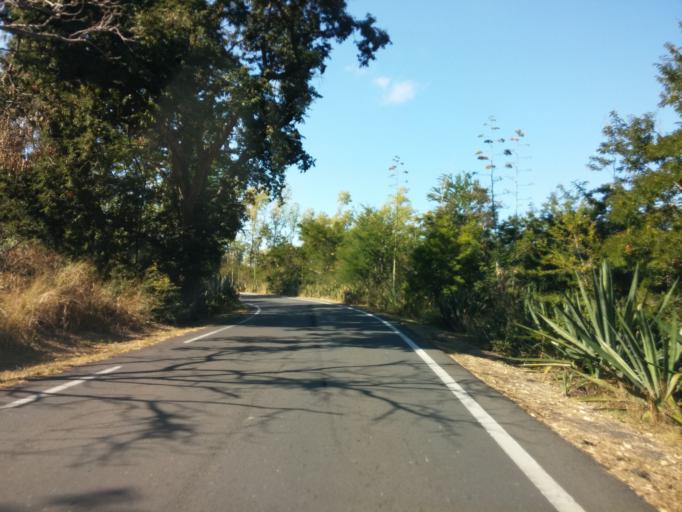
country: RE
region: Reunion
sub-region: Reunion
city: Les Avirons
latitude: -21.2606
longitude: 55.3460
